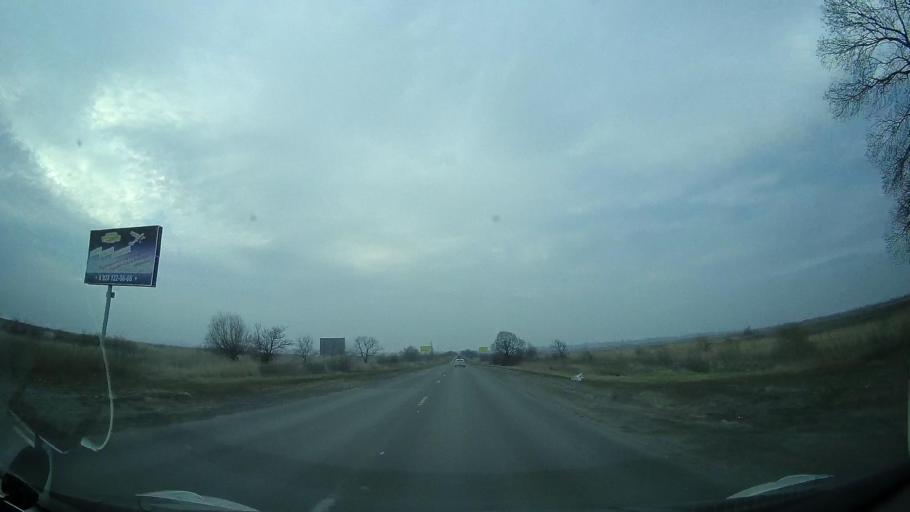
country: RU
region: Rostov
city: Ol'ginskaya
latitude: 47.2012
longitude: 39.9325
